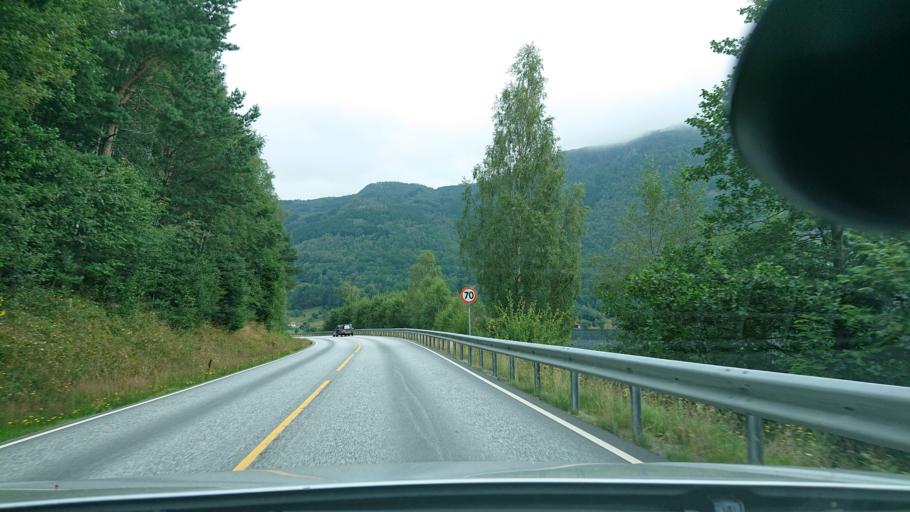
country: NO
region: Rogaland
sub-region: Hjelmeland
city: Hjelmelandsvagen
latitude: 59.1586
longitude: 6.1747
